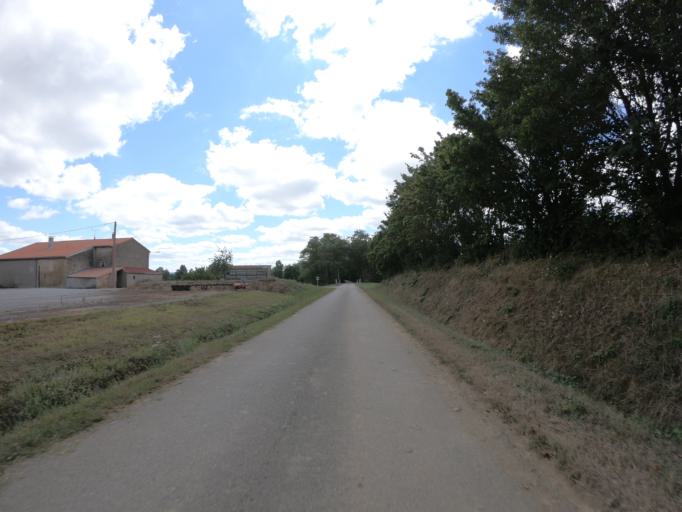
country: FR
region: Midi-Pyrenees
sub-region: Departement de l'Ariege
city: La Tour-du-Crieu
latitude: 43.1023
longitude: 1.7277
